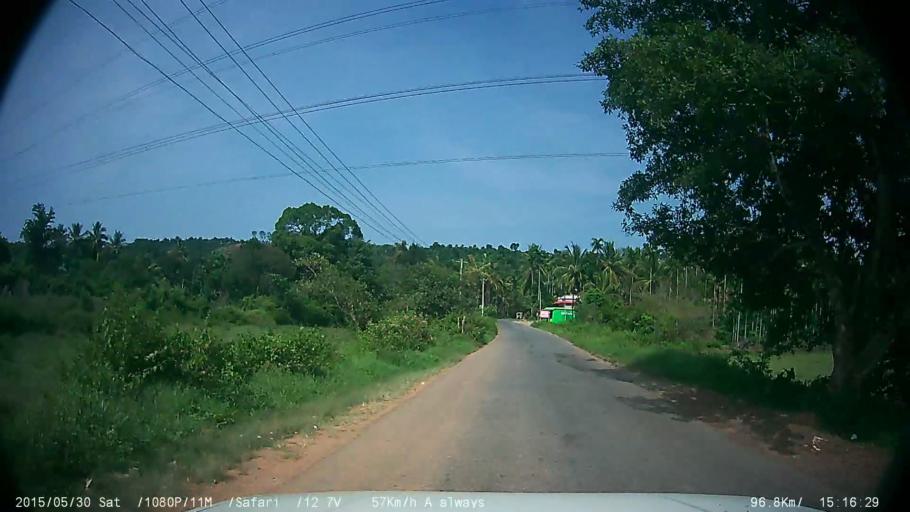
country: IN
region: Kerala
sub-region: Wayanad
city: Panamaram
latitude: 11.7762
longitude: 76.0553
